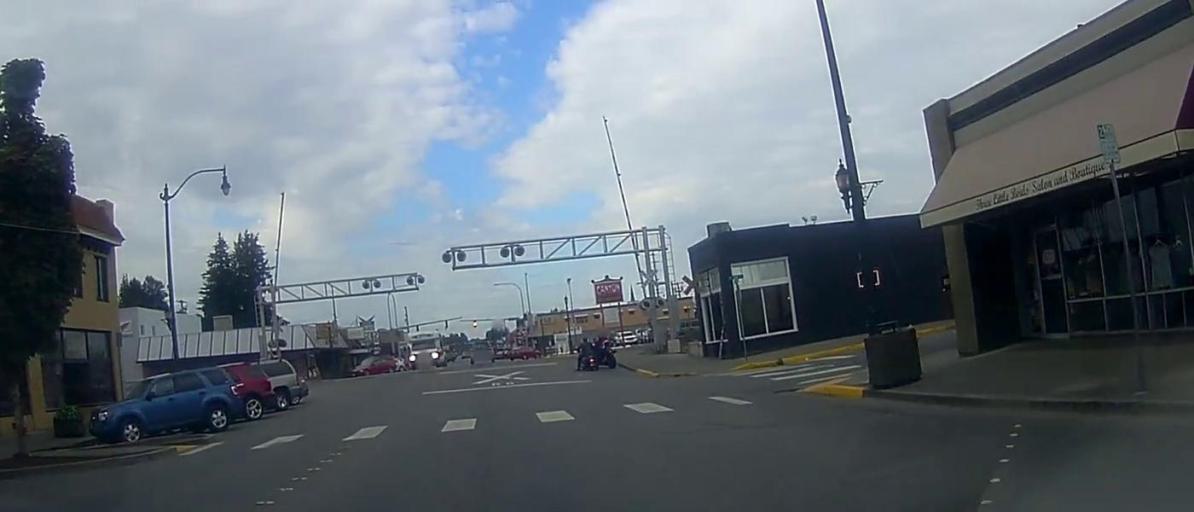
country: US
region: Washington
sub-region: Skagit County
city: Burlington
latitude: 48.4756
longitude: -122.3290
